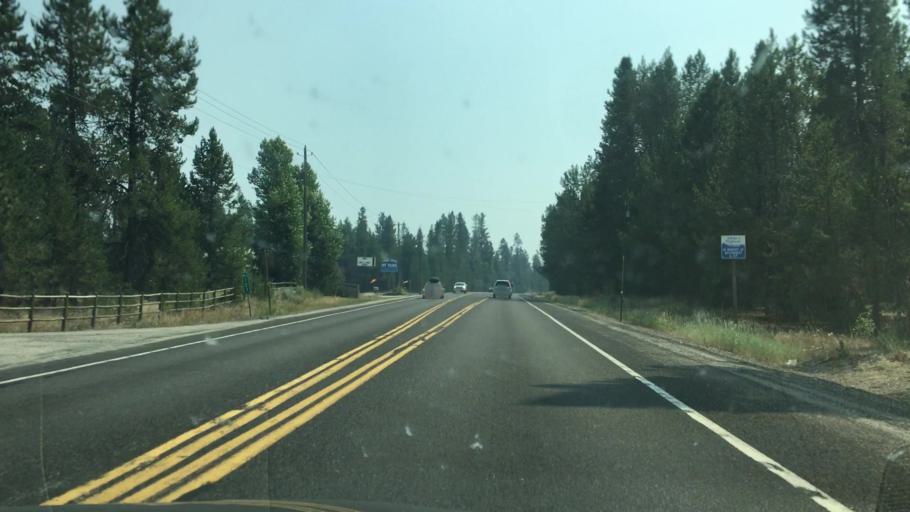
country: US
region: Idaho
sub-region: Valley County
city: Cascade
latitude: 44.4086
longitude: -115.9998
